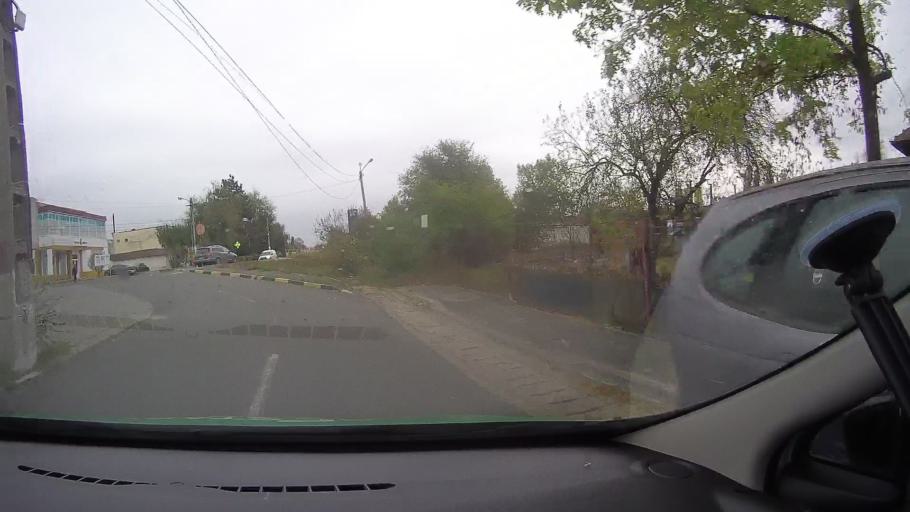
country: RO
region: Constanta
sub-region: Oras Murfatlar
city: Murfatlar
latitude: 44.1729
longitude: 28.4127
